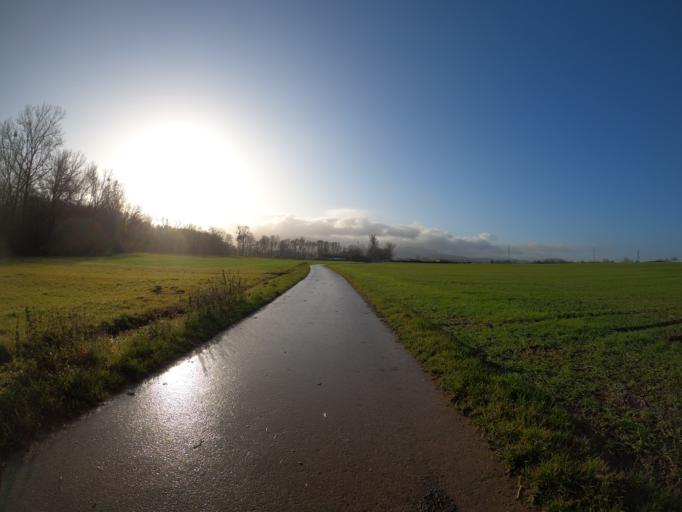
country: DE
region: Baden-Wuerttemberg
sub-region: Regierungsbezirk Stuttgart
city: Heiningen
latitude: 48.6688
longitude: 9.6248
